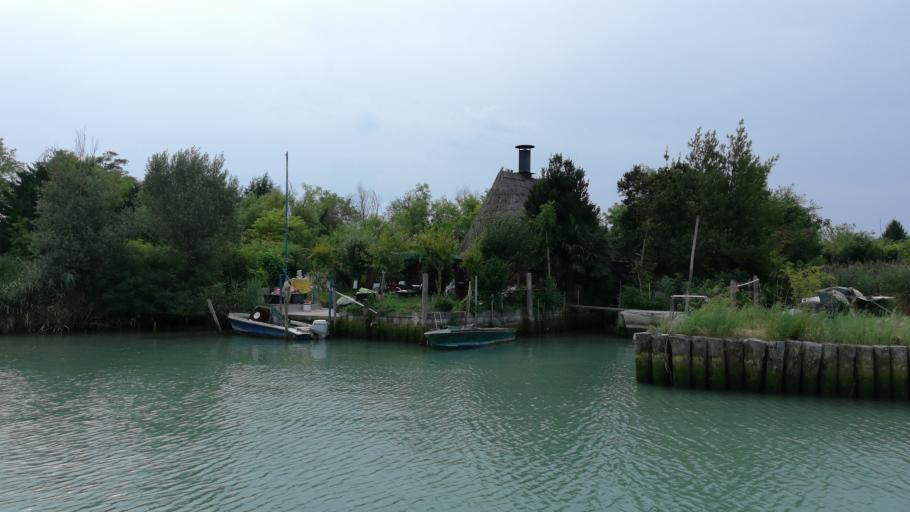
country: IT
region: Veneto
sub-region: Provincia di Venezia
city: Caorle
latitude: 45.6294
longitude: 12.8913
